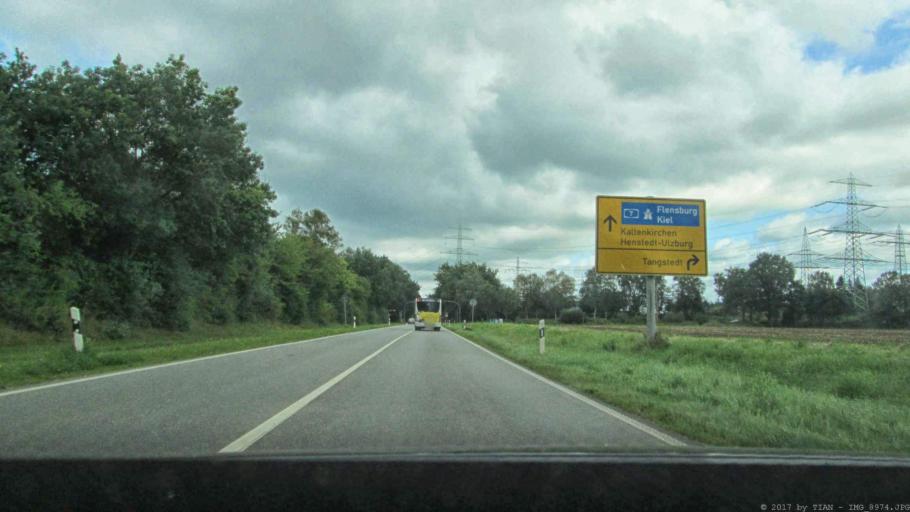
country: DE
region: Schleswig-Holstein
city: Tangstedt
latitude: 53.7246
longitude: 10.0262
